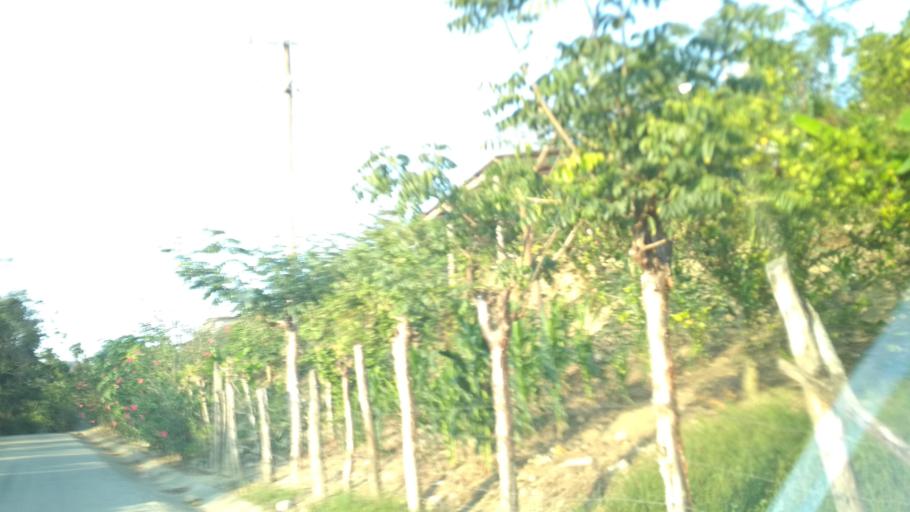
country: MX
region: Veracruz
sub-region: Poza Rica de Hidalgo
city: Arroyo del Maiz Uno
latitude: 20.4813
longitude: -97.3858
